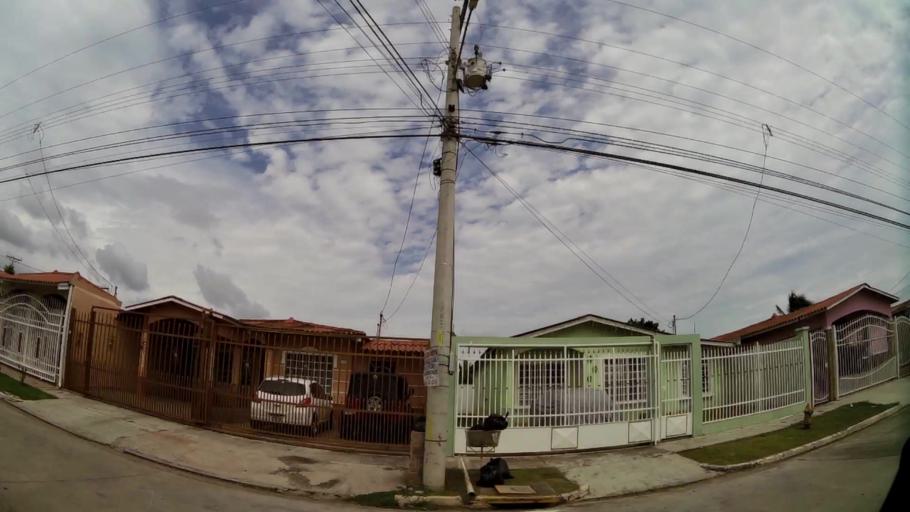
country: PA
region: Panama
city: Tocumen
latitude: 9.0452
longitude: -79.4132
